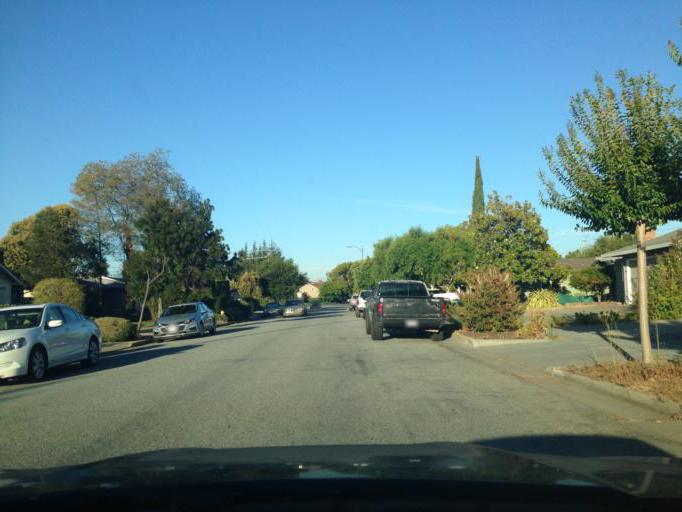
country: US
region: California
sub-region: Santa Clara County
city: Cambrian Park
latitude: 37.2338
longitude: -121.9056
